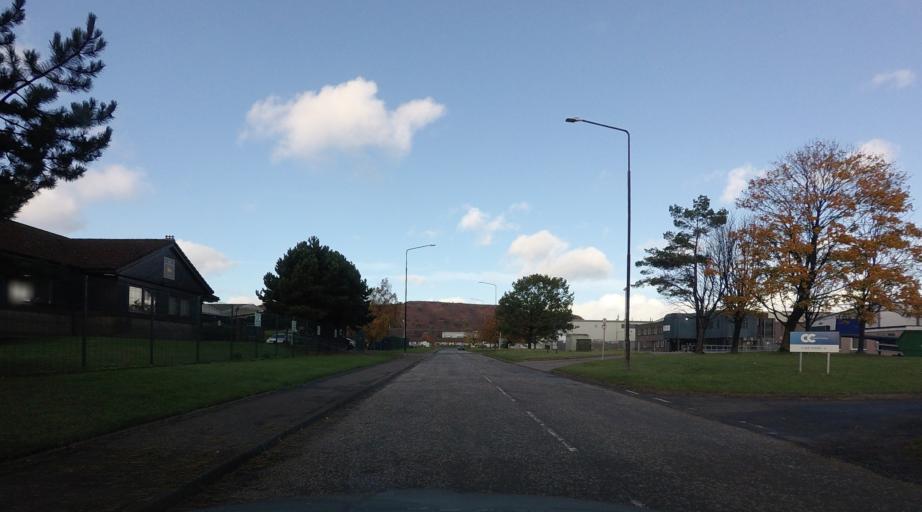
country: GB
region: Scotland
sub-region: West Lothian
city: Broxburn
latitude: 55.9387
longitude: -3.4534
